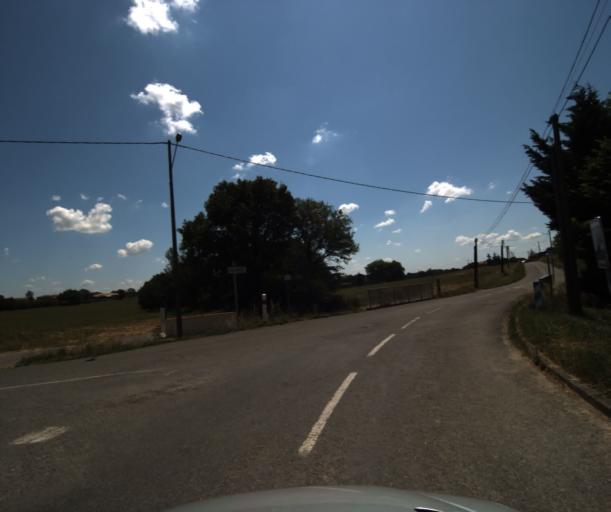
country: FR
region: Midi-Pyrenees
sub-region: Departement de la Haute-Garonne
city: Eaunes
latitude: 43.4205
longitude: 1.3485
